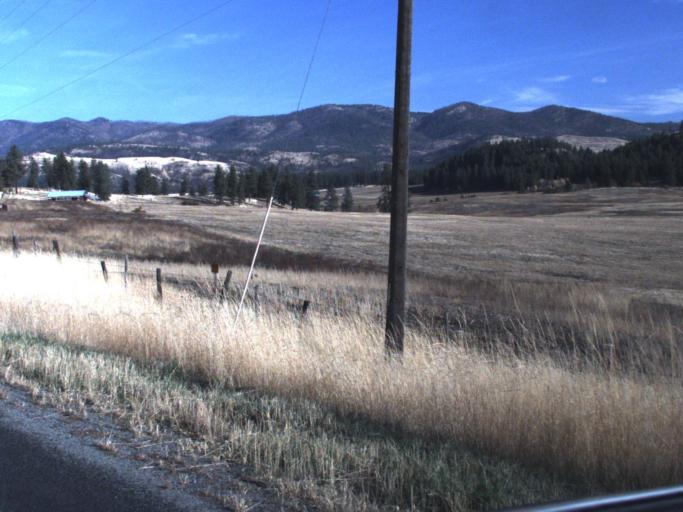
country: US
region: Washington
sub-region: Lincoln County
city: Davenport
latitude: 48.0063
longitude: -118.2694
